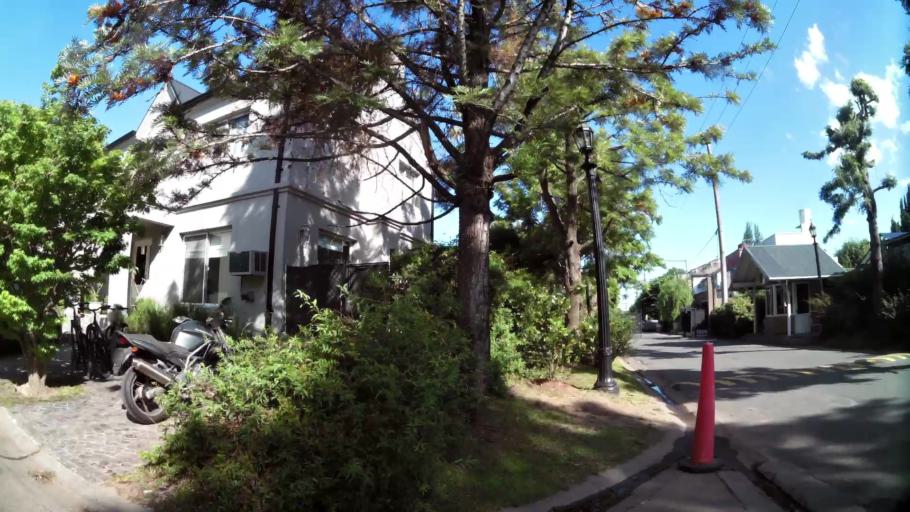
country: AR
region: Buenos Aires
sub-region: Partido de Tigre
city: Tigre
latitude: -34.4730
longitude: -58.5623
